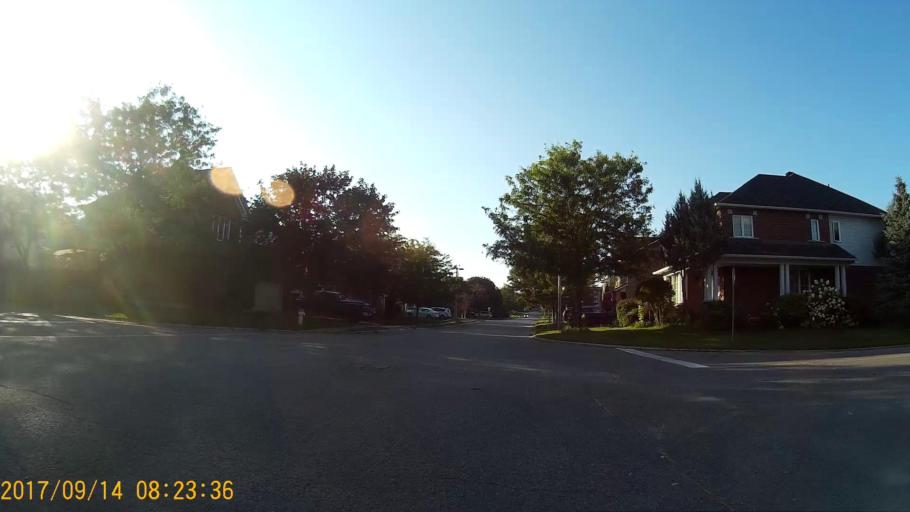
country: CA
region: Ontario
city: Bells Corners
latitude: 45.3508
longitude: -75.9302
